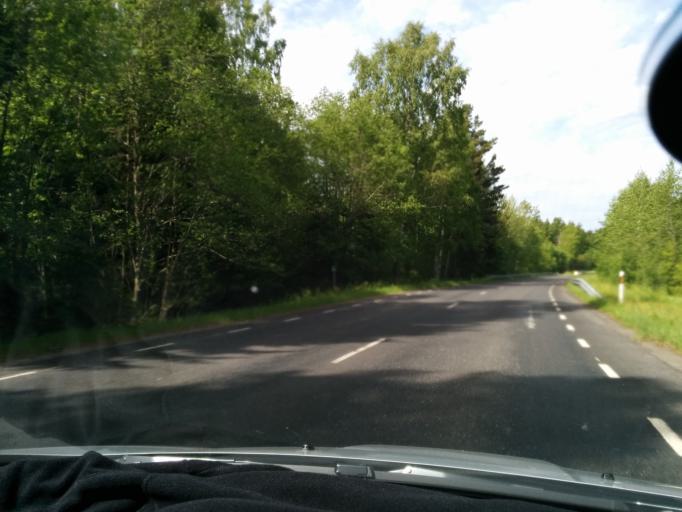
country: EE
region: Harju
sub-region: Loksa linn
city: Loksa
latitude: 59.5574
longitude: 25.7252
